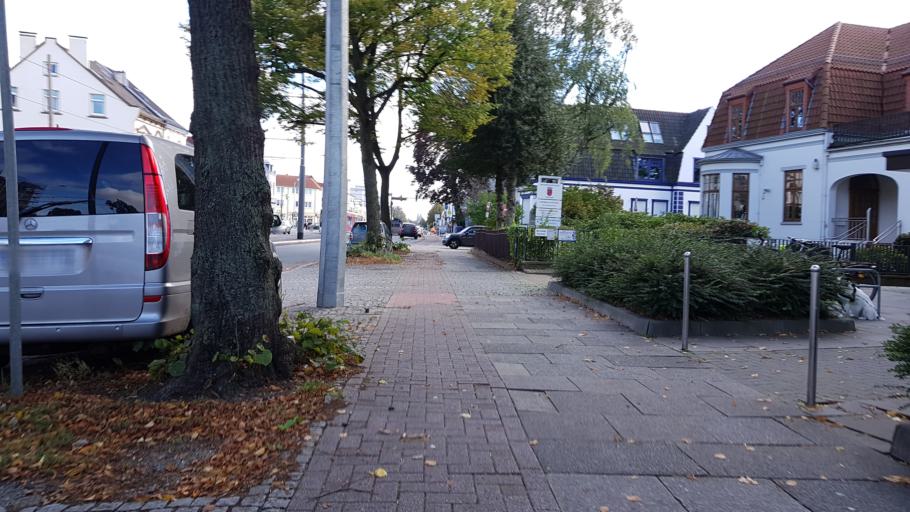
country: DE
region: Bremen
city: Bremen
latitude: 53.1036
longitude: 8.7840
